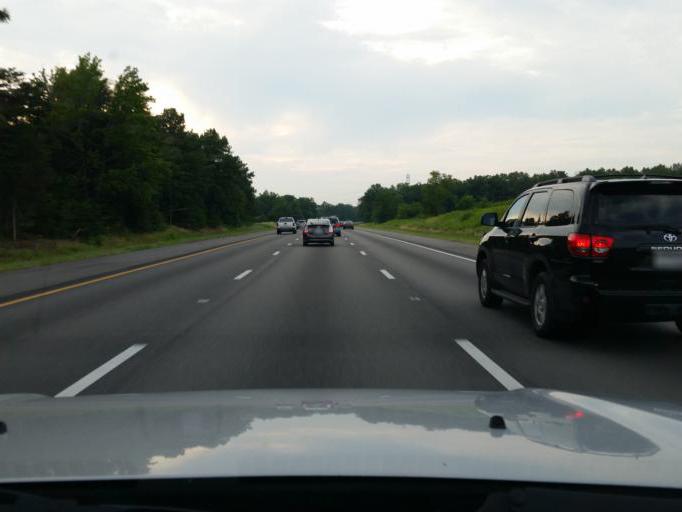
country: US
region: Virginia
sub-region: Spotsylvania County
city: Spotsylvania Courthouse
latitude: 38.0781
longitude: -77.5131
